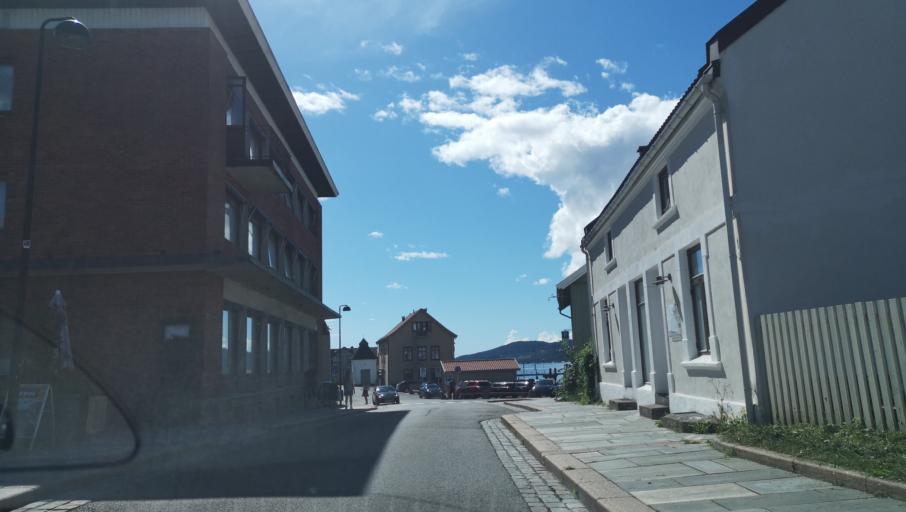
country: NO
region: Akershus
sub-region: Frogn
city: Drobak
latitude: 59.6598
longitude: 10.6303
